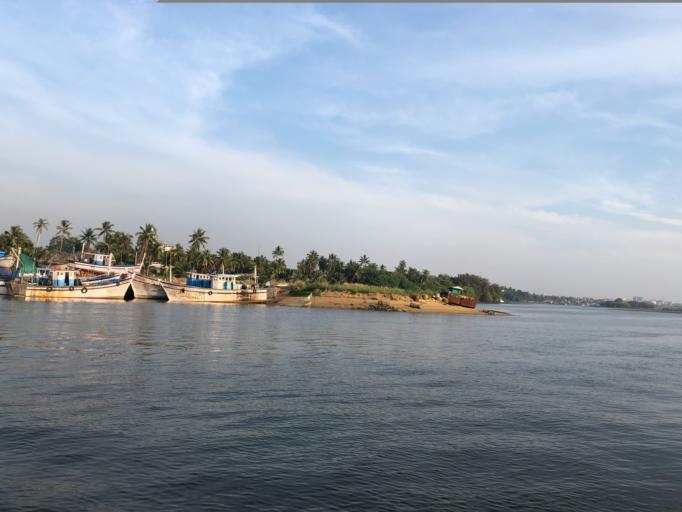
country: IN
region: Karnataka
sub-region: Dakshina Kannada
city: Mangalore
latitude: 12.8871
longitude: 74.8195
